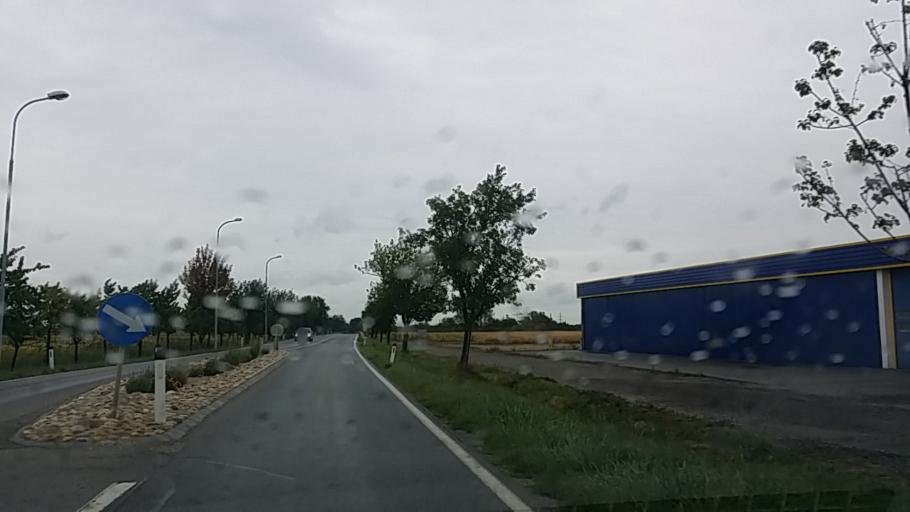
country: AT
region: Burgenland
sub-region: Eisenstadt-Umgebung
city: Schutzen am Gebirge
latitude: 47.8569
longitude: 16.6351
